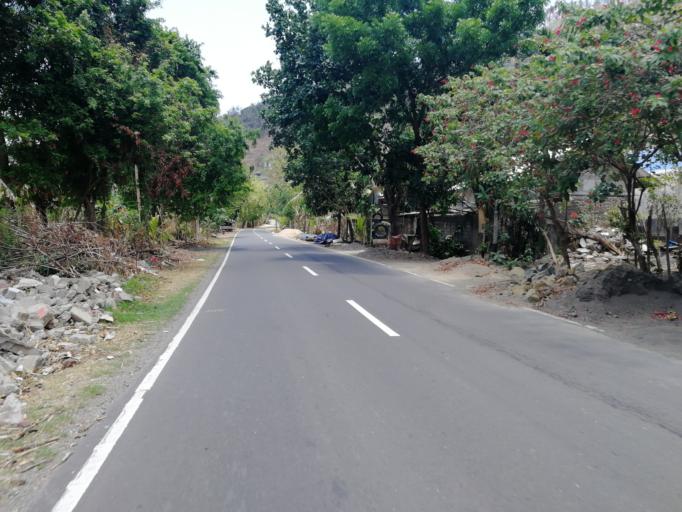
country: ID
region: West Nusa Tenggara
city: Karangsubagan
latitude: -8.4505
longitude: 116.0391
